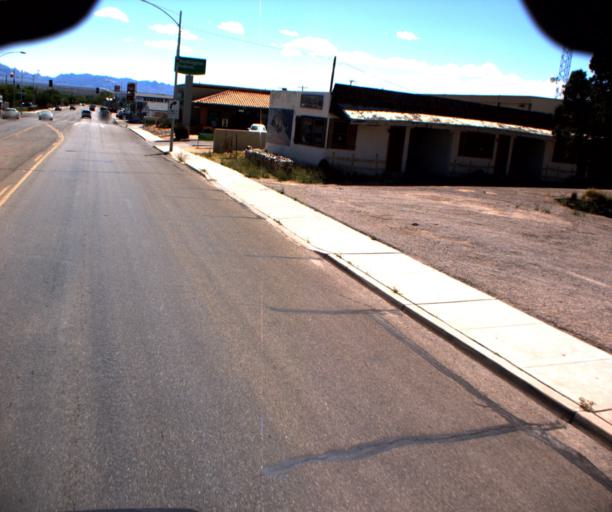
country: US
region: Arizona
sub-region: Cochise County
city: Benson
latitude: 31.9688
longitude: -110.2990
